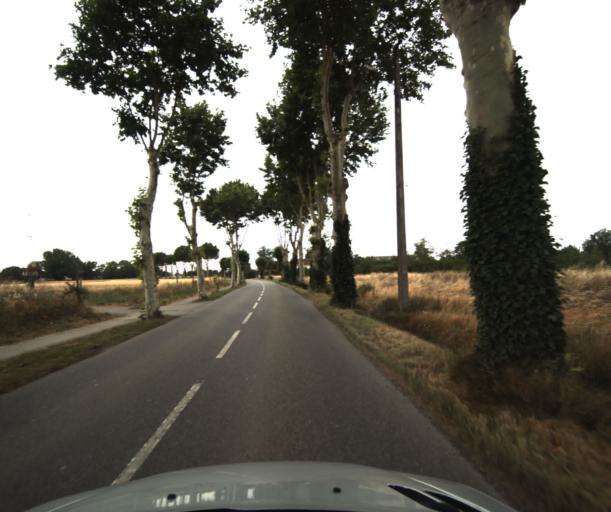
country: FR
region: Midi-Pyrenees
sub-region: Departement de la Haute-Garonne
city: Portet-sur-Garonne
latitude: 43.5296
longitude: 1.3963
